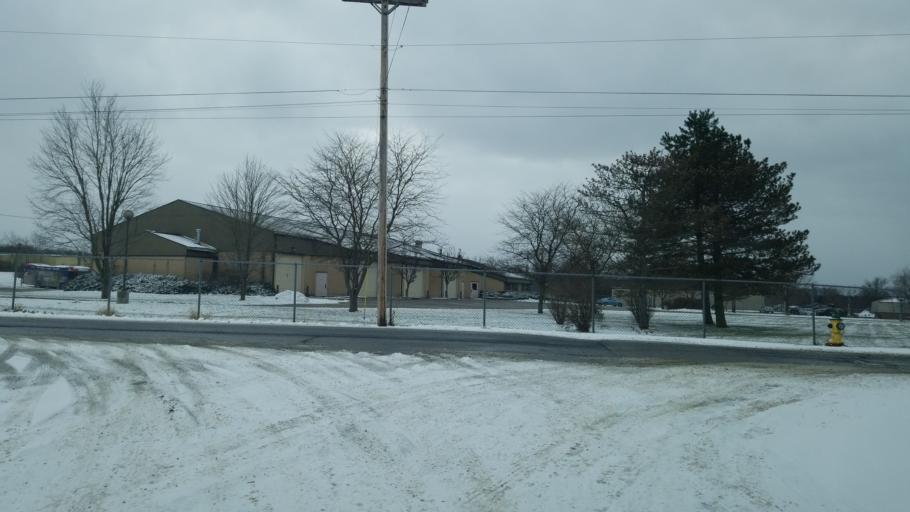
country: US
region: Pennsylvania
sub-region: Clearfield County
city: DuBois
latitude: 41.1101
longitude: -78.7315
